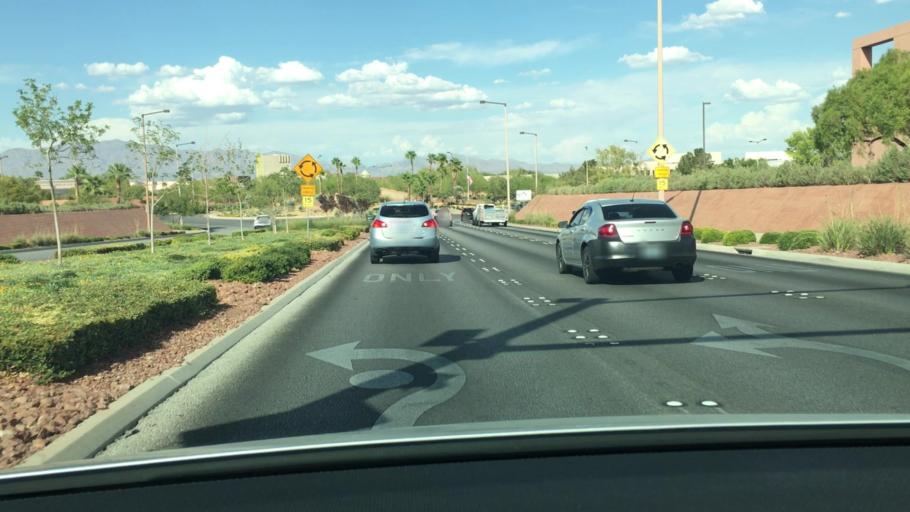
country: US
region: Nevada
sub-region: Clark County
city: Summerlin South
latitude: 36.1884
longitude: -115.3049
